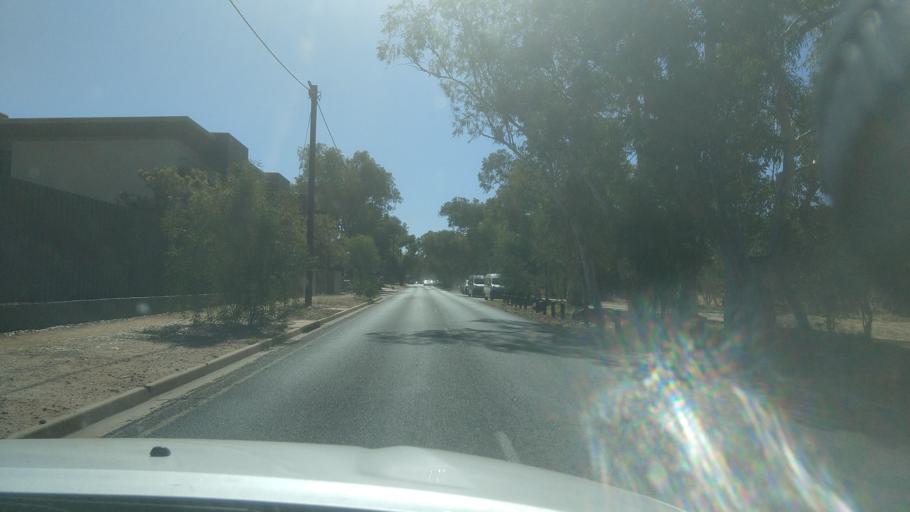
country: AU
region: Northern Territory
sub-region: Alice Springs
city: Alice Springs
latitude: -23.7134
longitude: 133.8771
